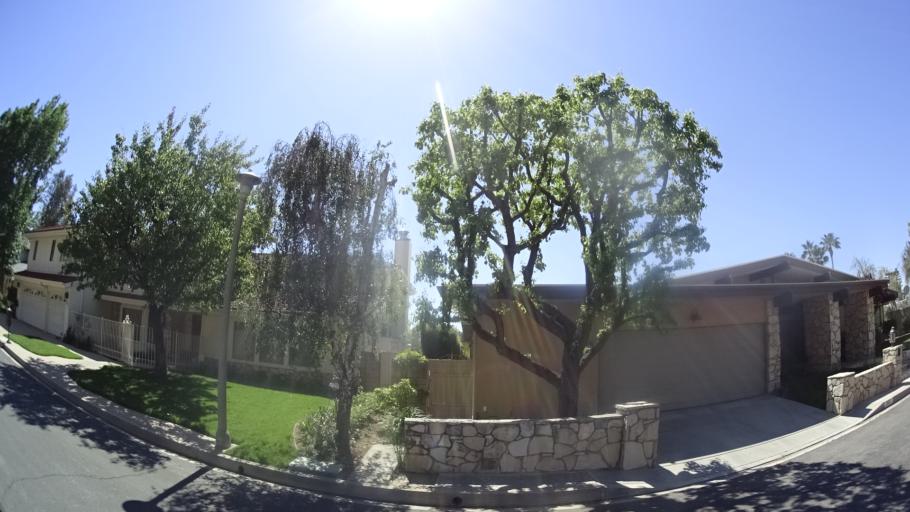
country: US
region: California
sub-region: Los Angeles County
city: Sherman Oaks
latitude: 34.1400
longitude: -118.4952
